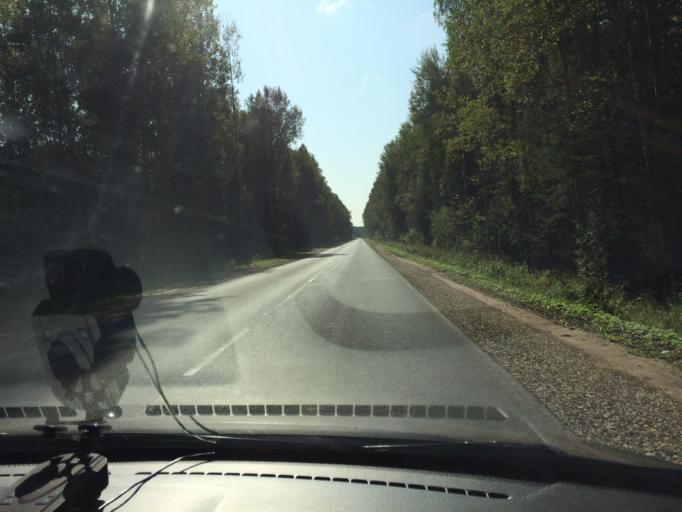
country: RU
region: Mariy-El
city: Surok
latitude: 56.5610
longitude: 48.3056
